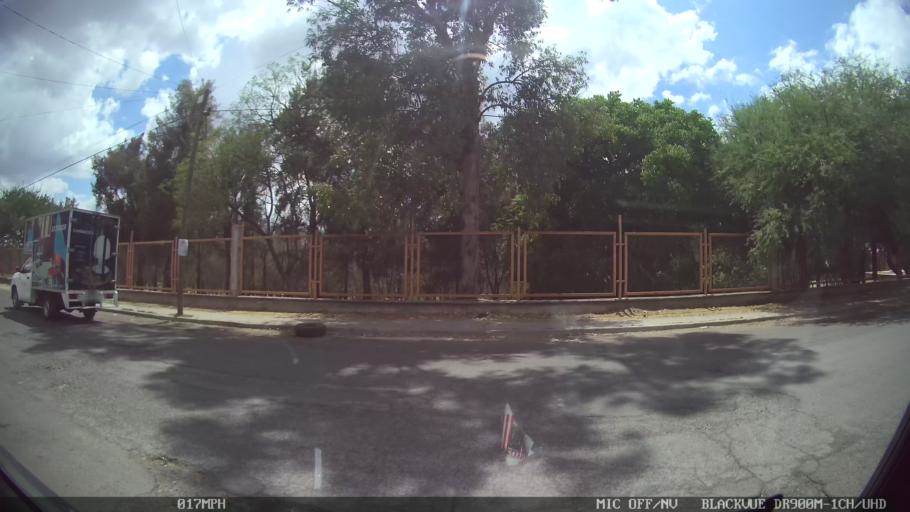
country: MX
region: Jalisco
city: Tlaquepaque
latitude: 20.6738
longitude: -103.2647
